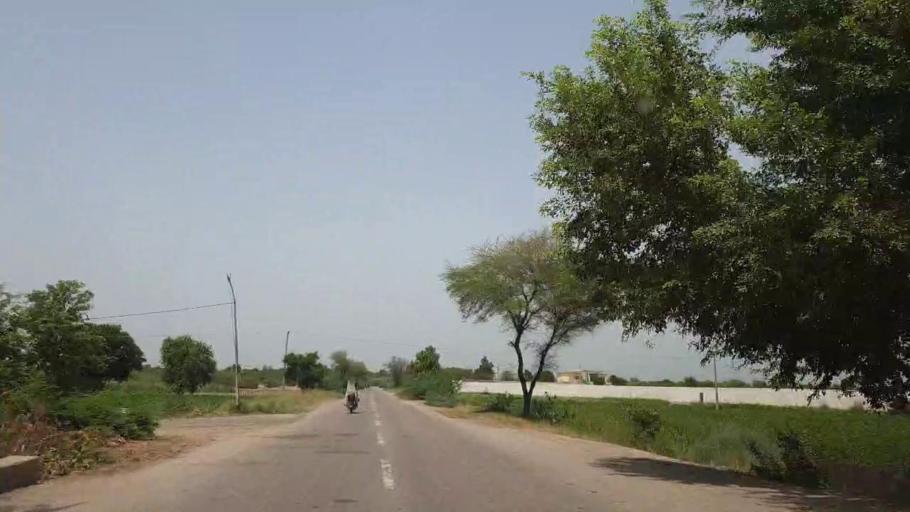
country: PK
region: Sindh
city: Sakrand
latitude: 26.1934
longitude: 68.2369
